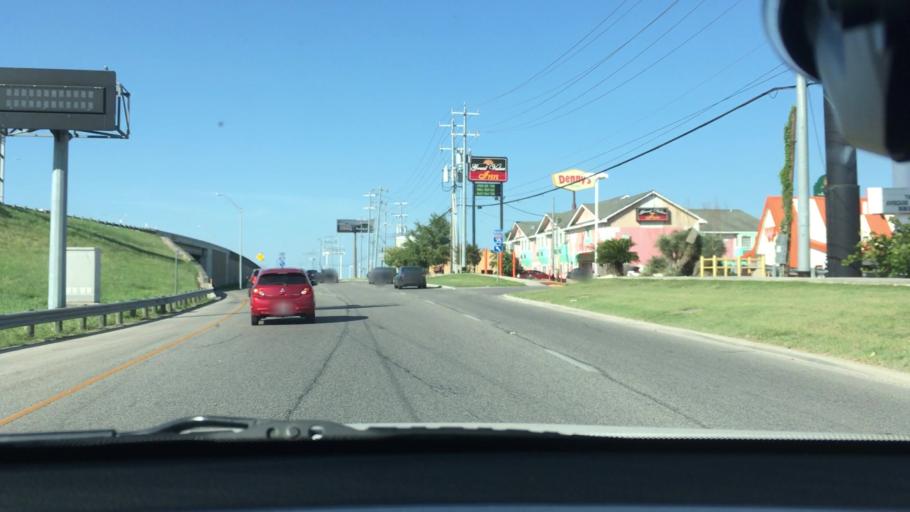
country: US
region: Texas
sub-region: Bexar County
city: Live Oak
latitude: 29.5549
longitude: -98.3476
